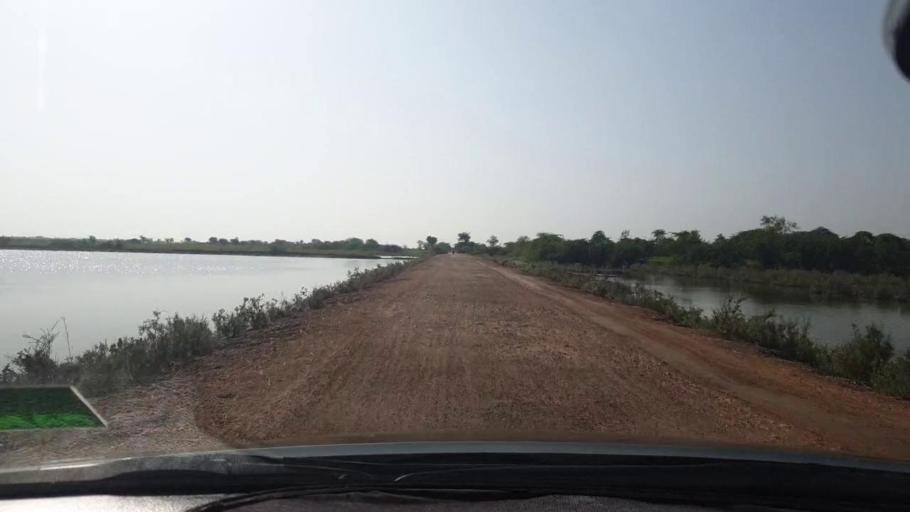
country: PK
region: Sindh
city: Tando Bago
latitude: 24.7228
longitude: 68.9580
